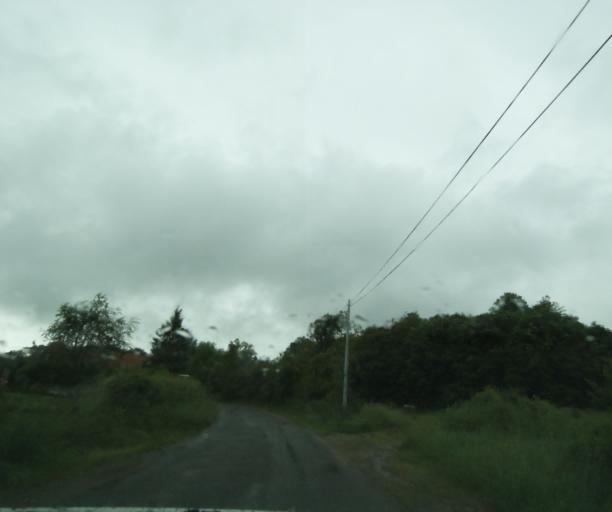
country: FR
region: Bourgogne
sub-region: Departement de Saone-et-Loire
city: Ciry-le-Noble
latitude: 46.5263
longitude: 4.3034
